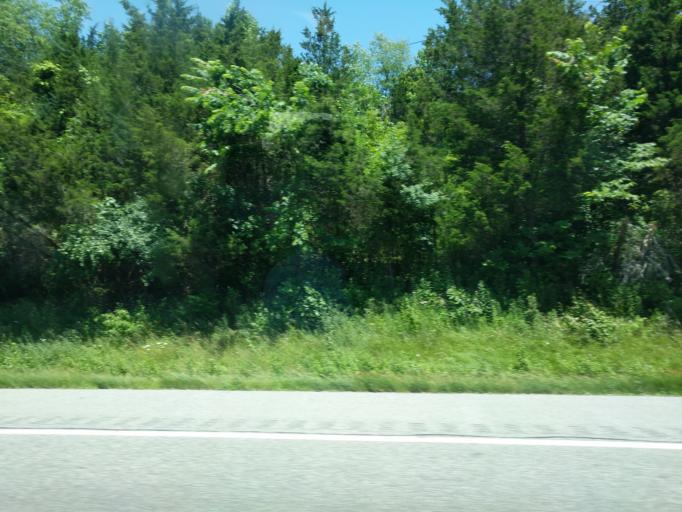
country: US
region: New York
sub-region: Orange County
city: Kiryas Joel
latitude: 41.3281
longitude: -74.1614
